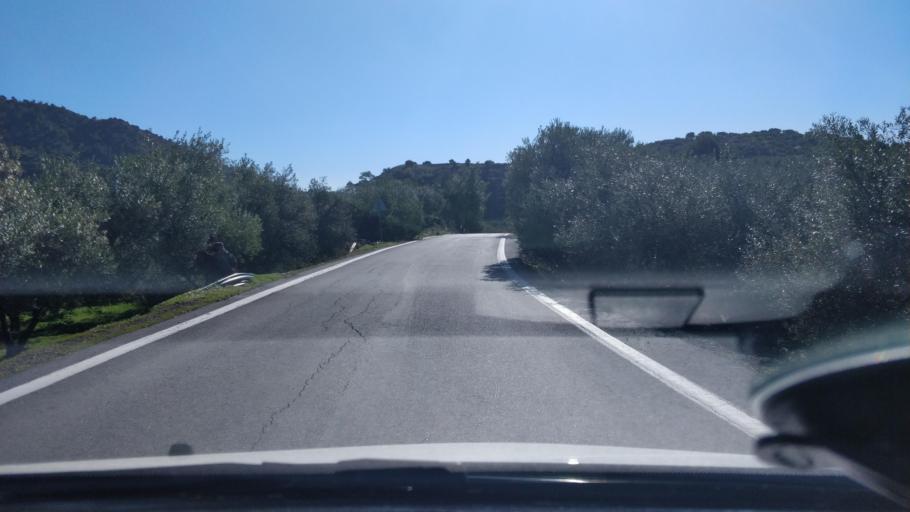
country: GR
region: Crete
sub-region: Nomos Irakleiou
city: Kastelli
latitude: 35.0196
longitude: 25.4489
